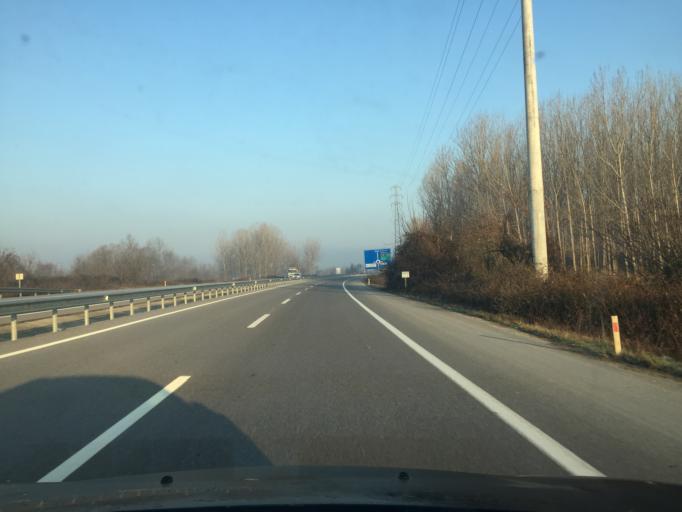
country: TR
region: Sakarya
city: Akyazi
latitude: 40.6550
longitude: 30.5995
